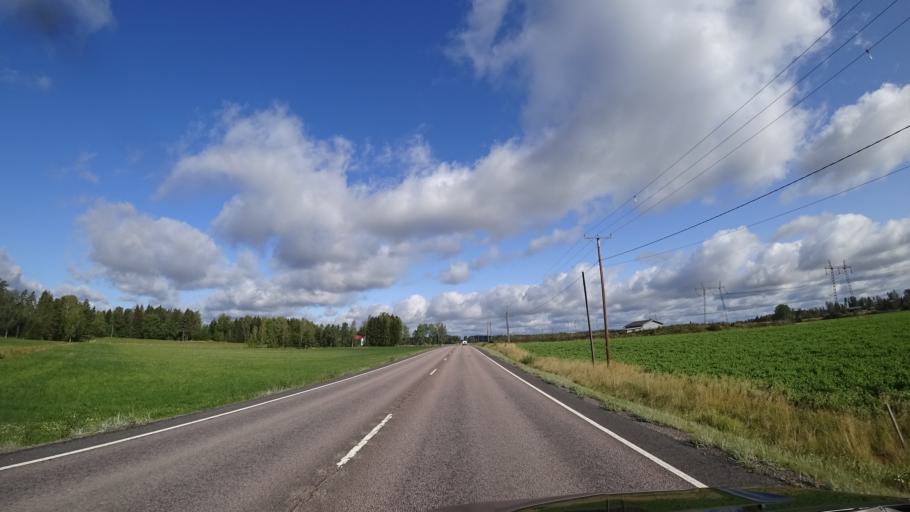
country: FI
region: Uusimaa
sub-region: Helsinki
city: Nurmijaervi
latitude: 60.5133
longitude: 24.9273
